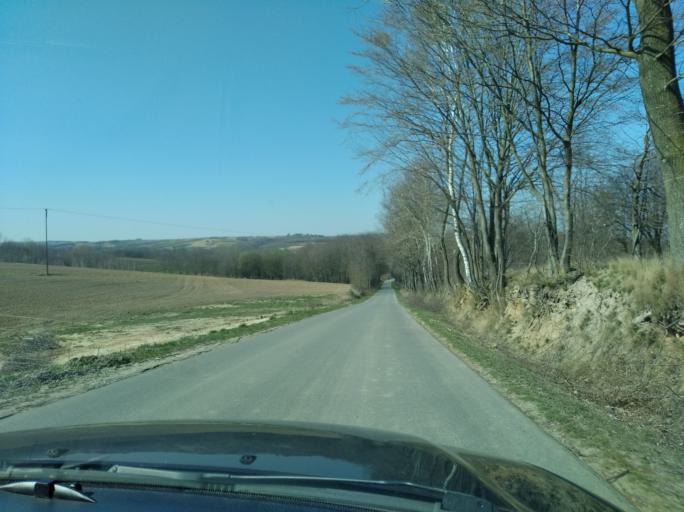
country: PL
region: Subcarpathian Voivodeship
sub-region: Powiat przeworski
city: Pantalowice
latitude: 49.9258
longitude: 22.4520
